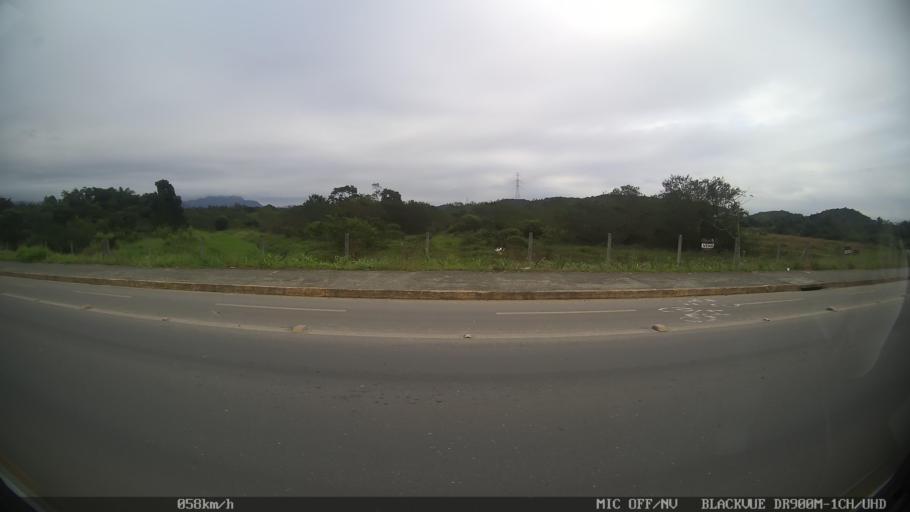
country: BR
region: Santa Catarina
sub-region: Joinville
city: Joinville
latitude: -26.3377
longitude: -48.8912
